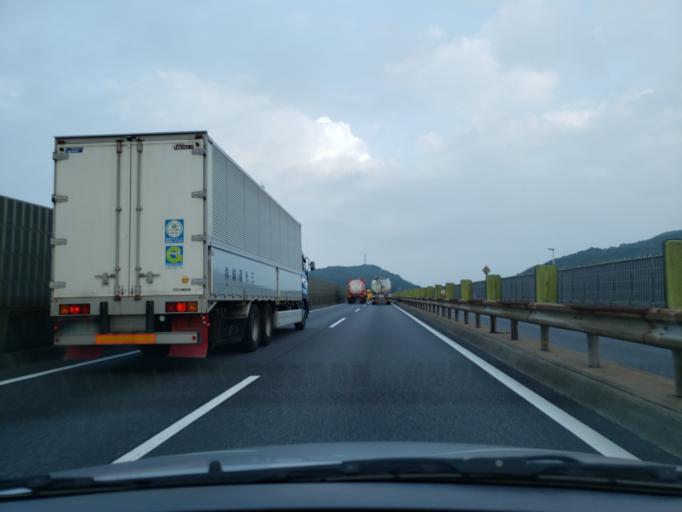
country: JP
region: Hyogo
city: Tatsunocho-tominaga
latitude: 34.8476
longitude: 134.5871
